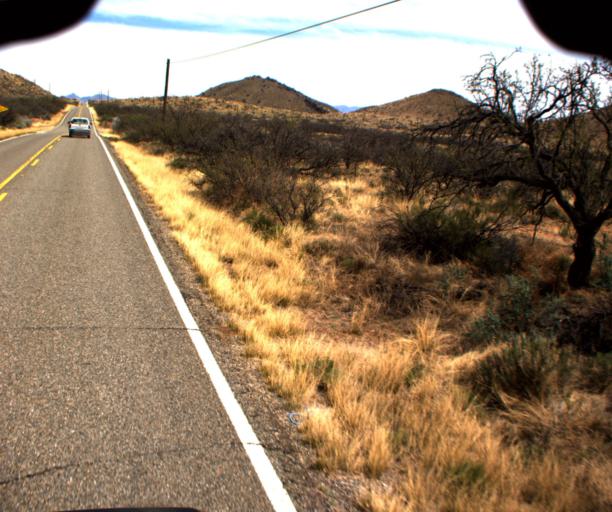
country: US
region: Arizona
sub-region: Cochise County
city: Willcox
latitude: 32.1714
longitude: -109.5986
